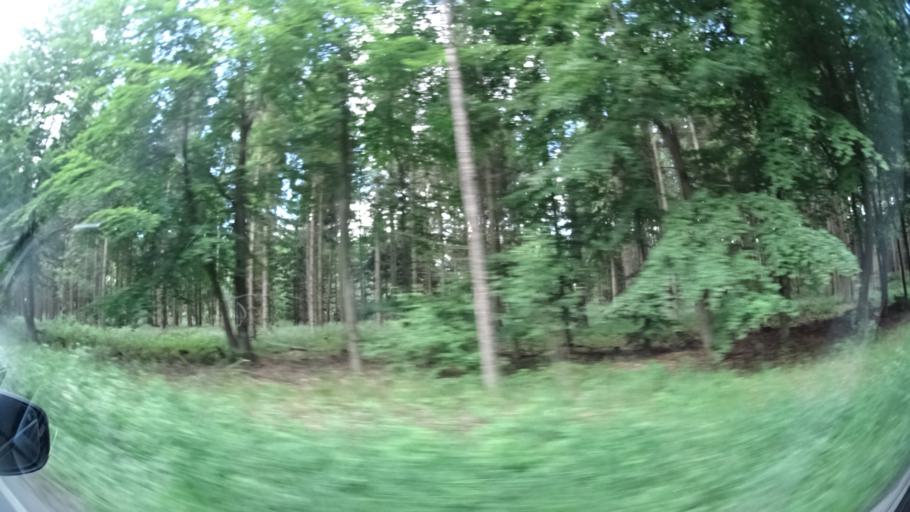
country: DK
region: Central Jutland
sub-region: Syddjurs Kommune
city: Ebeltoft
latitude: 56.2528
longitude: 10.6386
